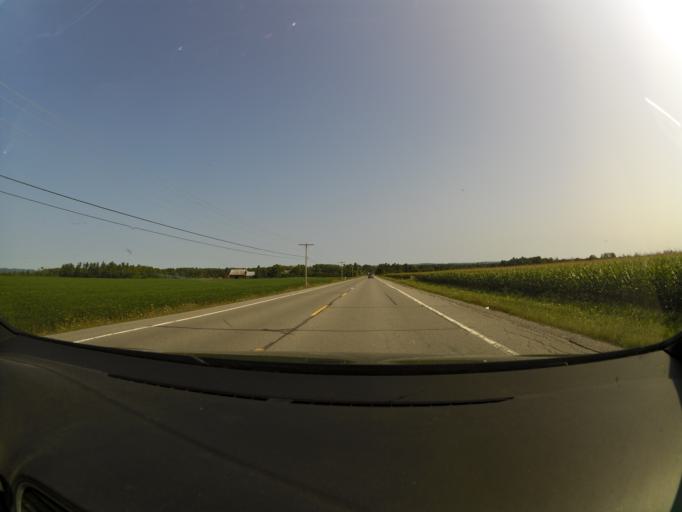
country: CA
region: Ontario
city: Arnprior
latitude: 45.4885
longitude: -76.1517
